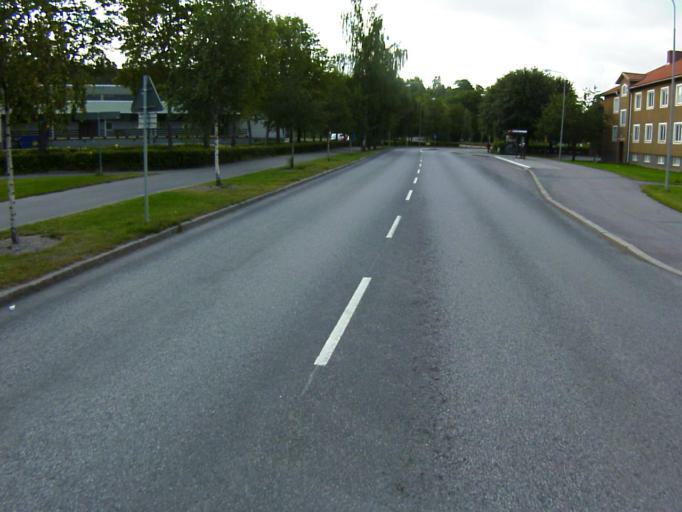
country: SE
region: Soedermanland
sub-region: Eskilstuna Kommun
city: Eskilstuna
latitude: 59.3634
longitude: 16.5292
